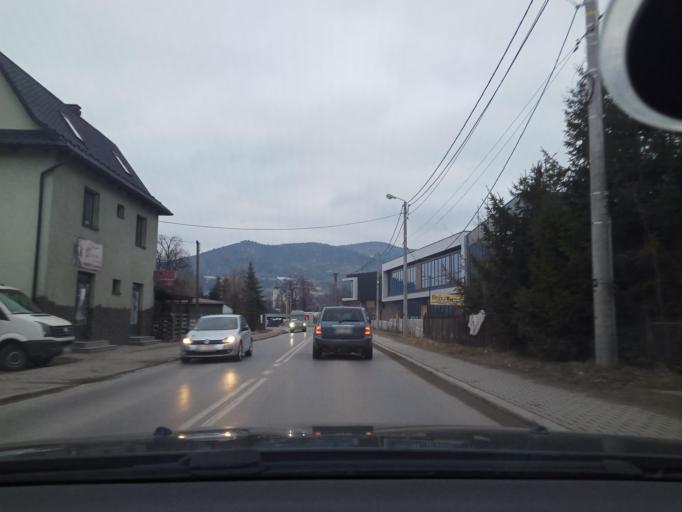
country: PL
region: Lesser Poland Voivodeship
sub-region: Powiat limanowski
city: Mszana Dolna
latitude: 49.6700
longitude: 20.0842
